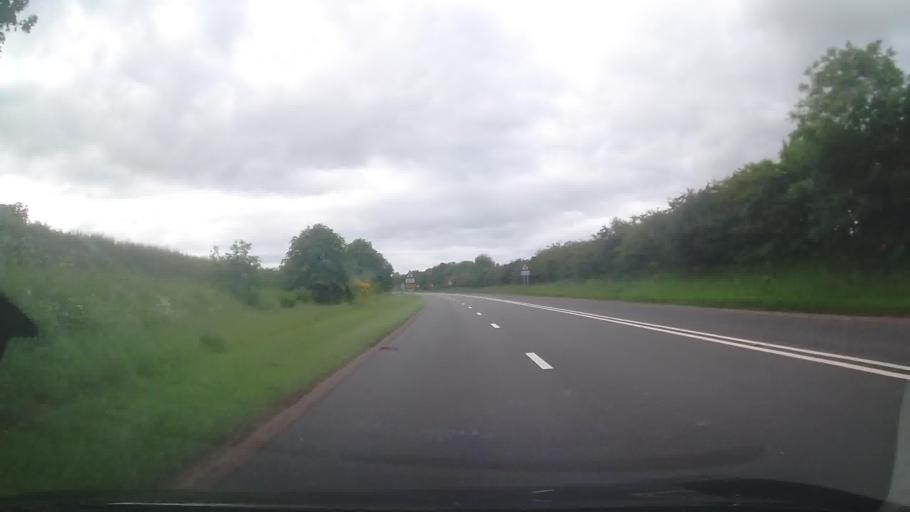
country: GB
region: England
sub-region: Shropshire
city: Stoke upon Tern
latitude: 52.8352
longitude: -2.4611
